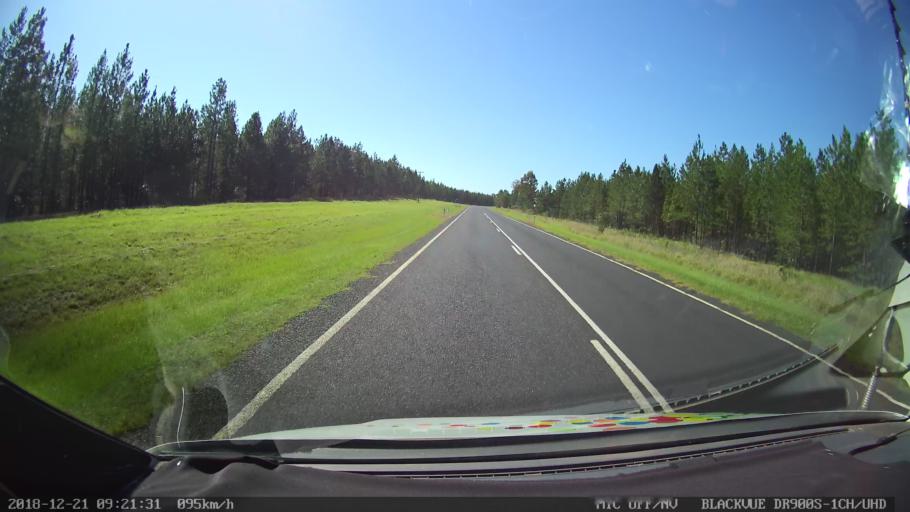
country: AU
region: New South Wales
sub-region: Clarence Valley
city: Maclean
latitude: -29.3300
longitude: 152.9985
